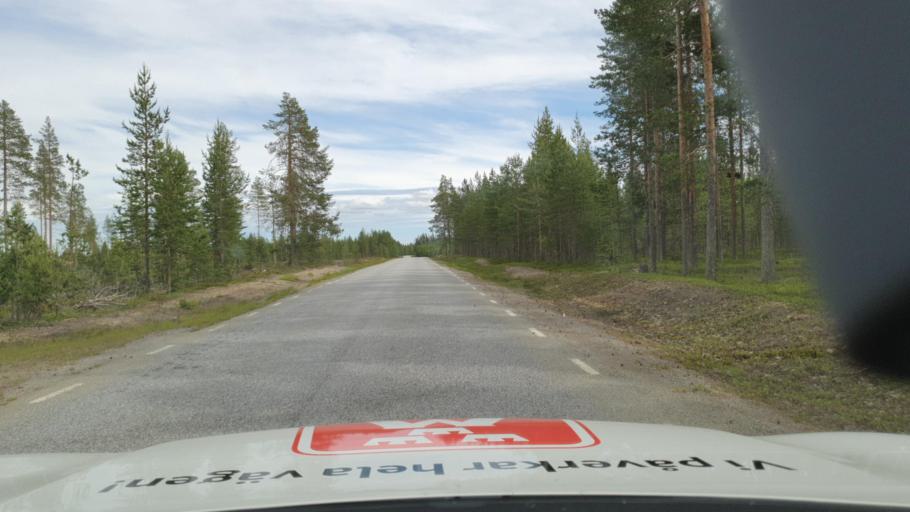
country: SE
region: Vaesterbotten
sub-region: Skelleftea Kommun
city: Burtraesk
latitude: 64.5039
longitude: 20.8194
